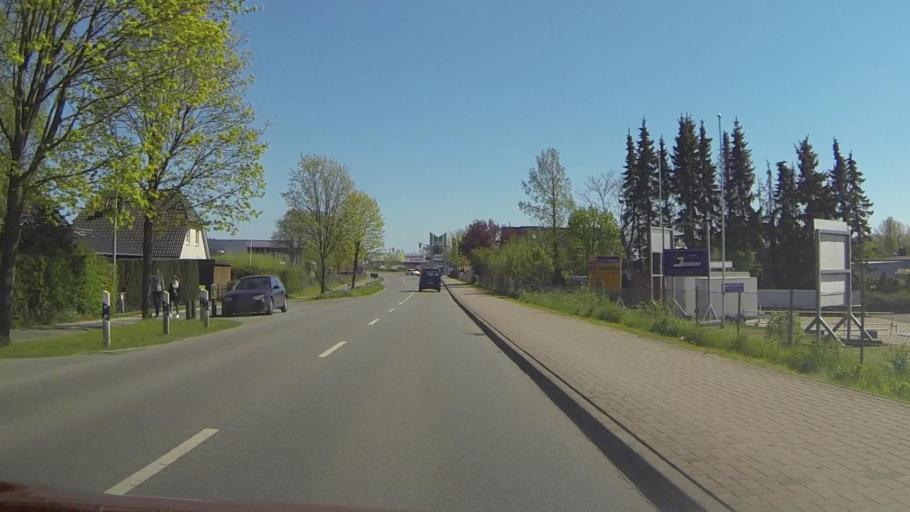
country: DE
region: Schleswig-Holstein
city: Kummerfeld
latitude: 53.6748
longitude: 9.7711
